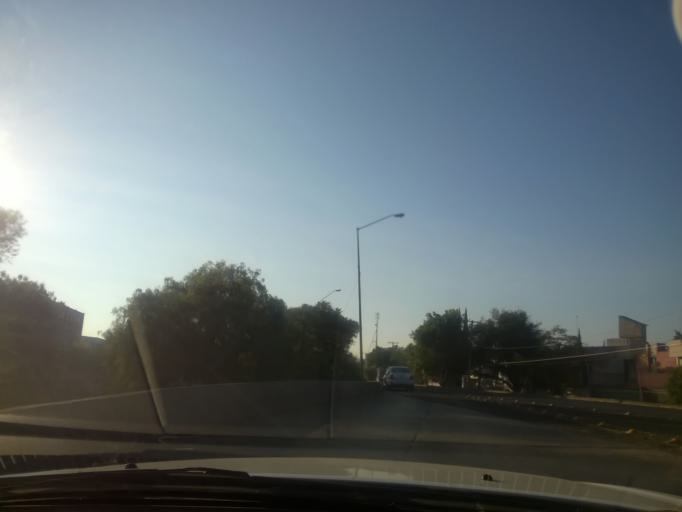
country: MX
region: Guanajuato
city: Leon
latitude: 21.1070
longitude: -101.6625
